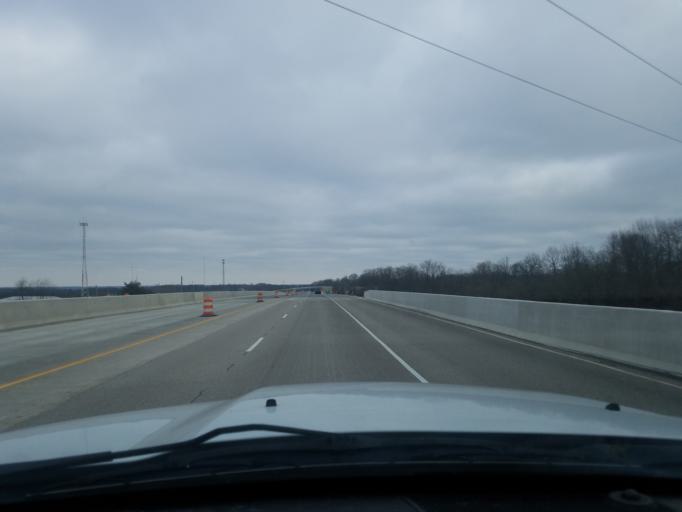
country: US
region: Indiana
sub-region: Monroe County
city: Bloomington
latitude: 39.1727
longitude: -86.5675
